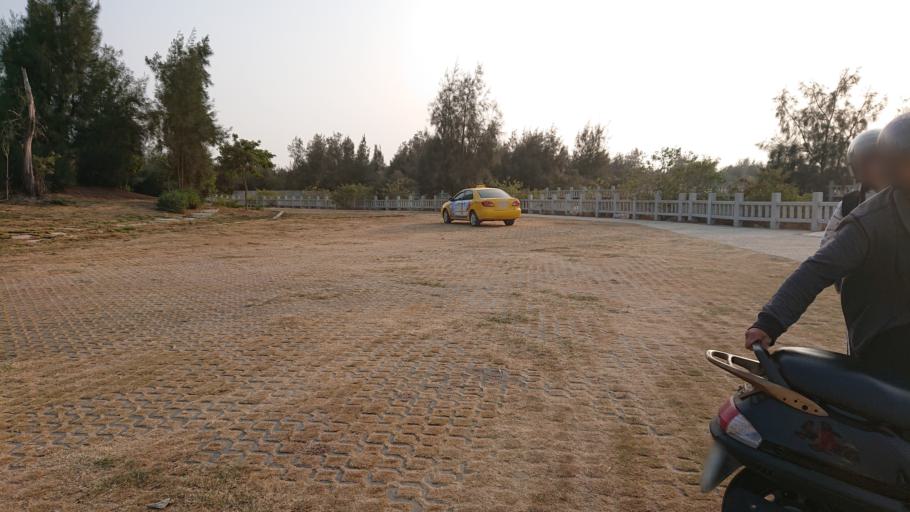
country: TW
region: Fukien
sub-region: Kinmen
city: Jincheng
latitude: 24.4285
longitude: 118.2270
